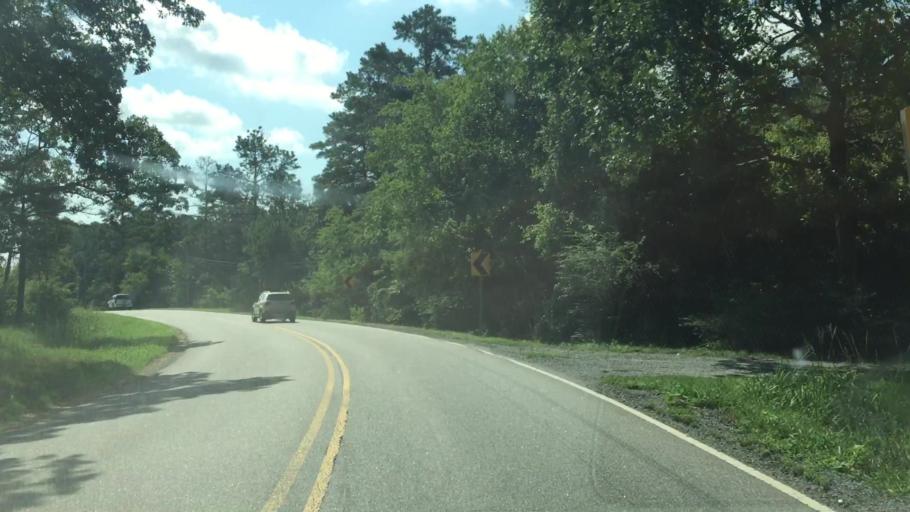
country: US
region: North Carolina
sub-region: Anson County
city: Polkton
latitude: 35.0316
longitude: -80.2422
